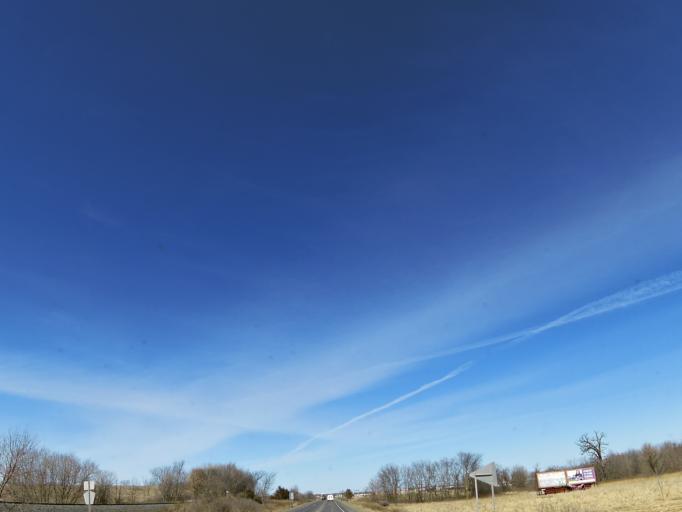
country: US
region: Minnesota
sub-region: Wright County
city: Buffalo
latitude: 45.1464
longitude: -93.8388
